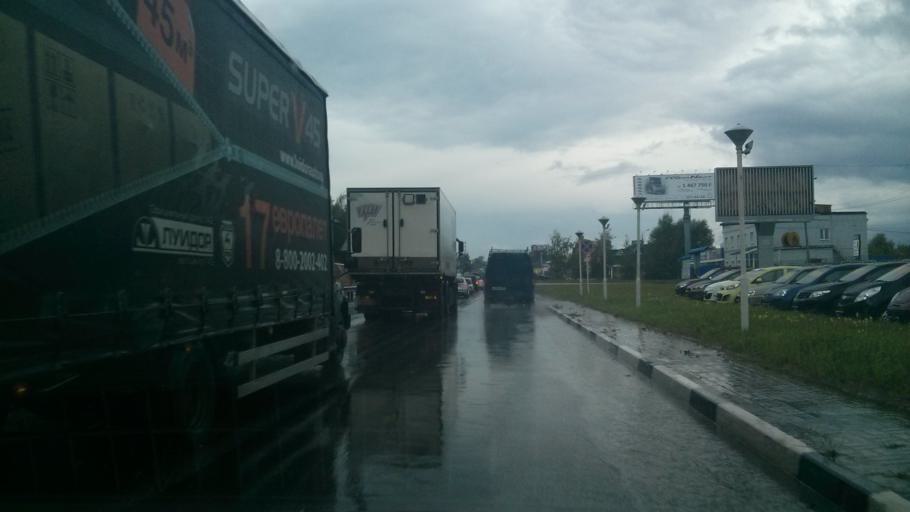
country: RU
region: Nizjnij Novgorod
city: Afonino
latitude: 56.2369
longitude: 44.0141
